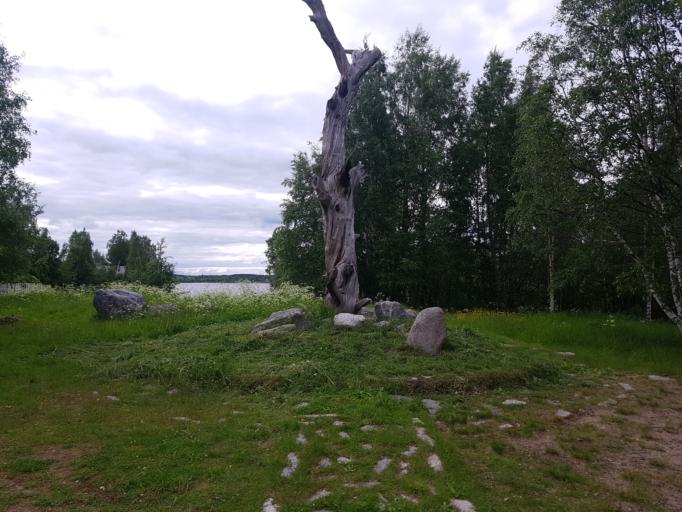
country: RU
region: Republic of Karelia
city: Kalevala
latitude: 65.1948
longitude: 31.1824
